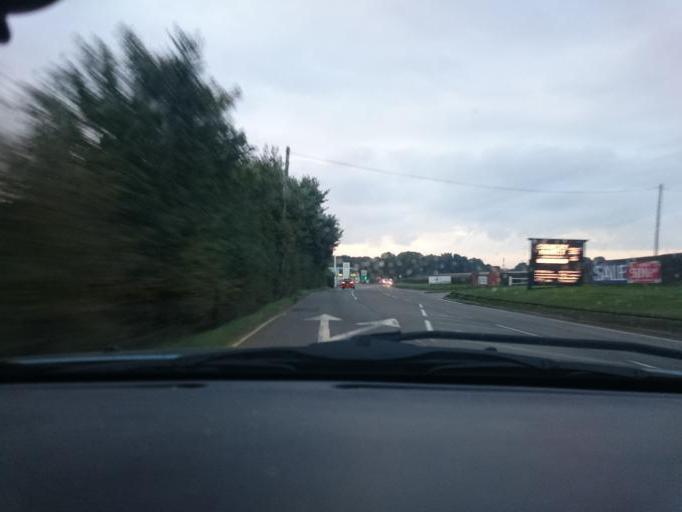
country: GB
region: England
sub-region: Hampshire
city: Lindford
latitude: 51.1420
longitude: -0.8517
